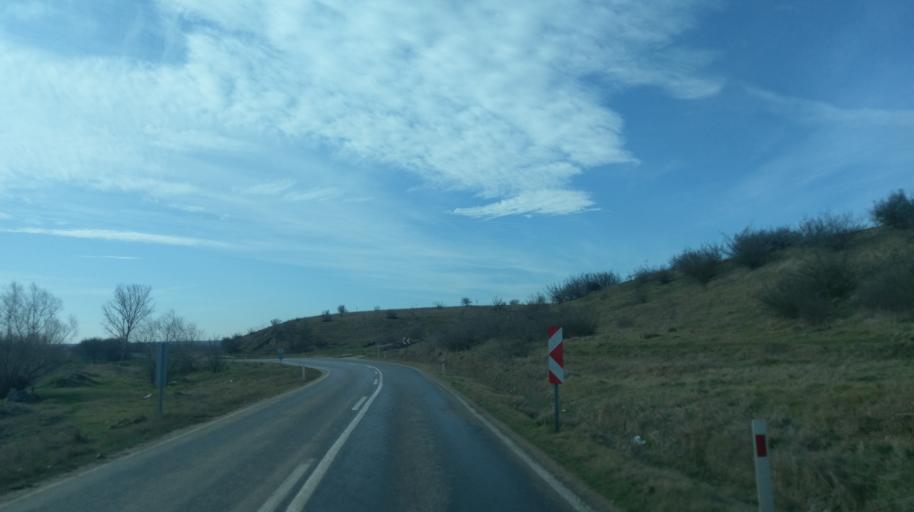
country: TR
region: Kirklareli
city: Pehlivankoy
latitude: 41.3796
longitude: 26.9892
